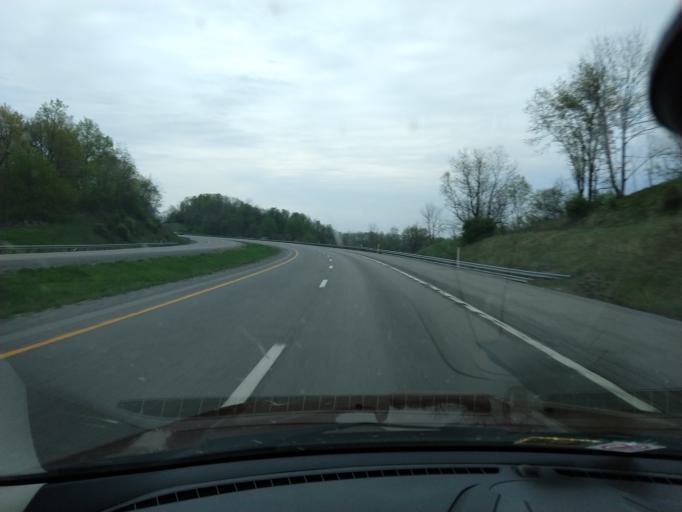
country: US
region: West Virginia
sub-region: Lewis County
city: Weston
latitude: 38.9291
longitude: -80.5446
